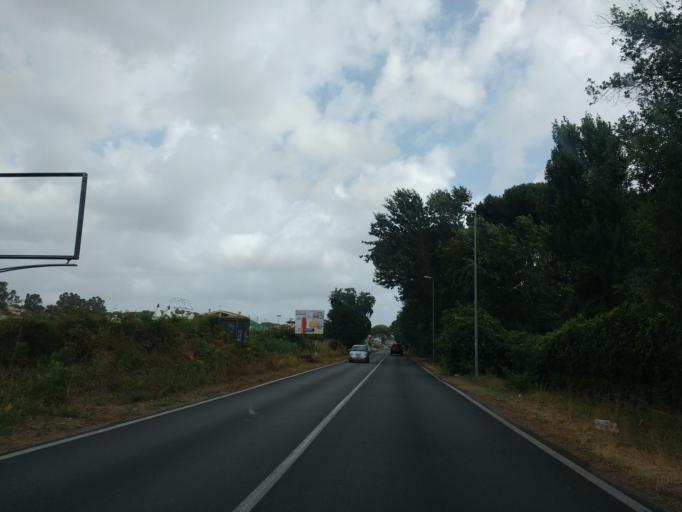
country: IT
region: Latium
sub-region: Citta metropolitana di Roma Capitale
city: Lavinio
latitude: 41.4930
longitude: 12.5944
